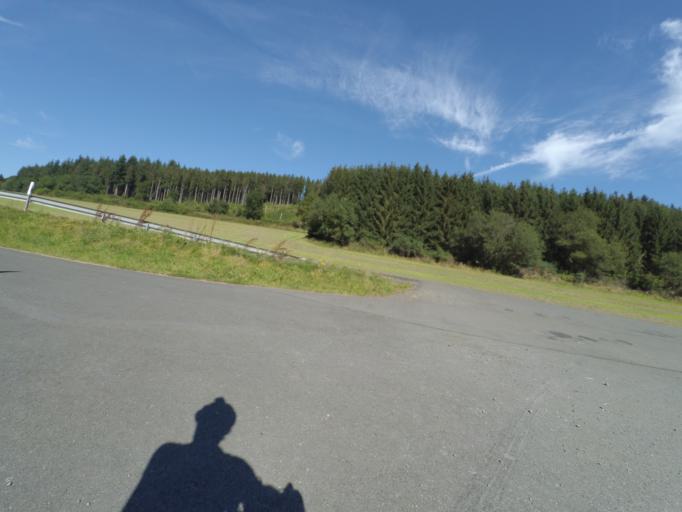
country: DE
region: Rheinland-Pfalz
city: Oberstadtfeld
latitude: 50.1845
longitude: 6.7898
